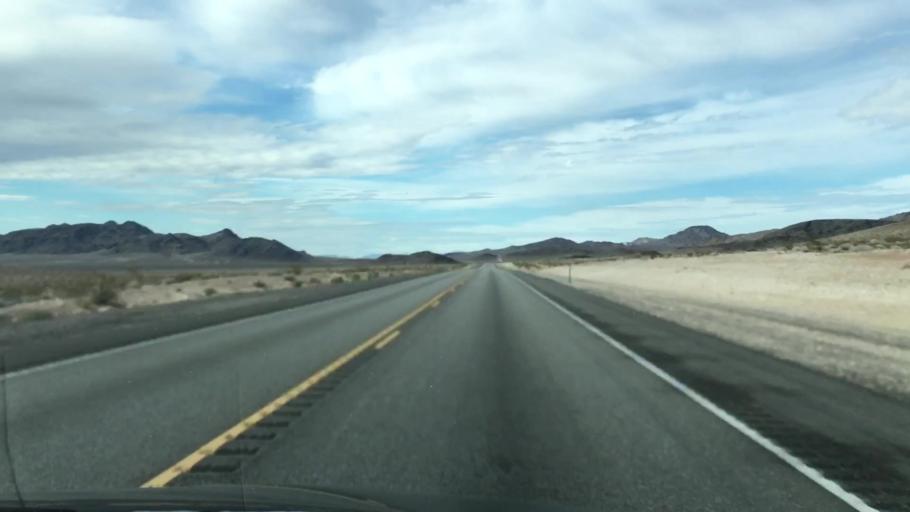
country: US
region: Nevada
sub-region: Nye County
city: Pahrump
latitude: 36.6134
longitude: -116.2775
